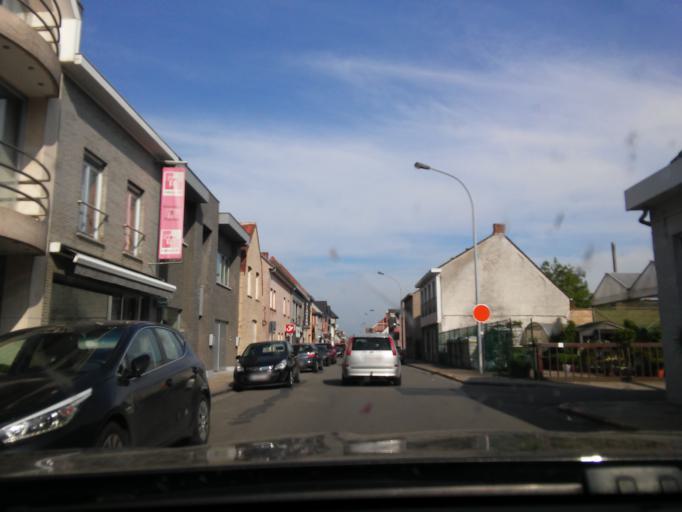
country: BE
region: Flanders
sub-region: Provincie Oost-Vlaanderen
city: Sint-Laureins
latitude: 51.2432
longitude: 3.5194
